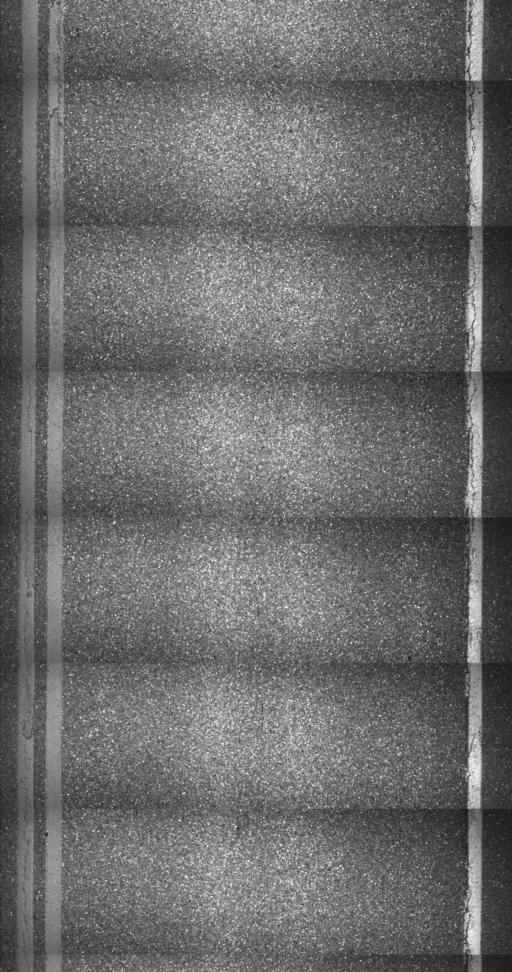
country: US
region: Vermont
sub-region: Rutland County
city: Fair Haven
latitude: 43.6957
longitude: -73.2939
